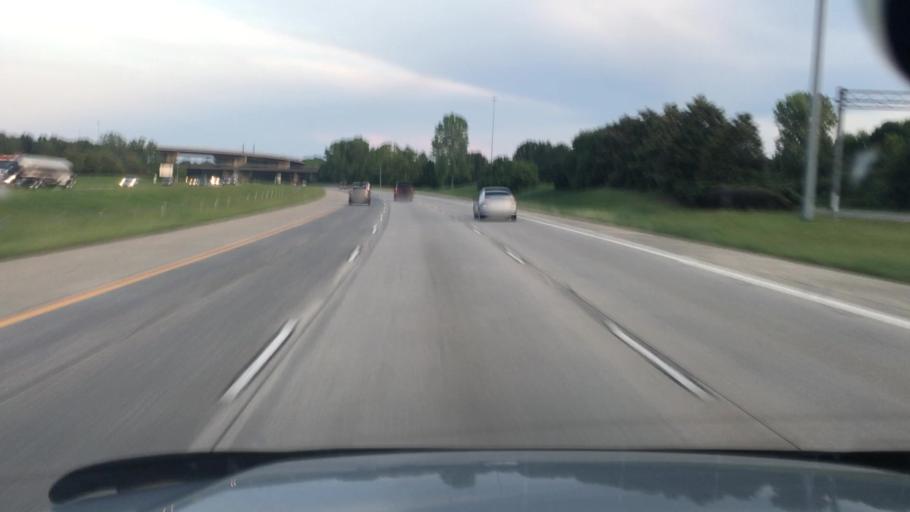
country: US
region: North Carolina
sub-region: Mecklenburg County
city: Pineville
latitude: 35.1287
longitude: -80.9216
